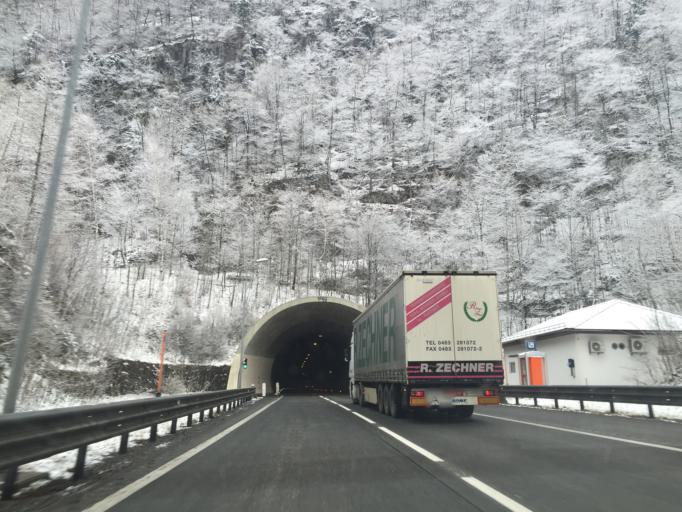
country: AT
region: Salzburg
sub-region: Politischer Bezirk Hallein
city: Golling an der Salzach
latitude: 47.5771
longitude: 13.1624
